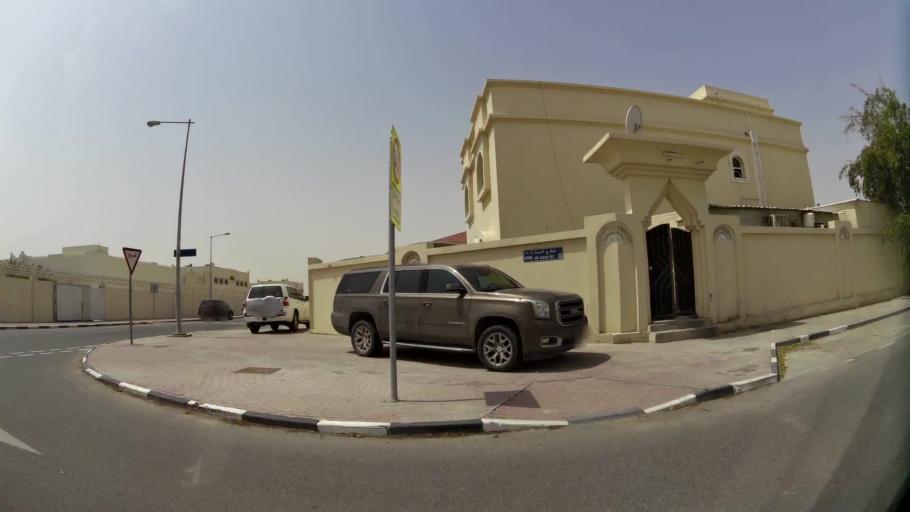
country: QA
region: Baladiyat ar Rayyan
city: Ar Rayyan
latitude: 25.2465
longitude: 51.4261
